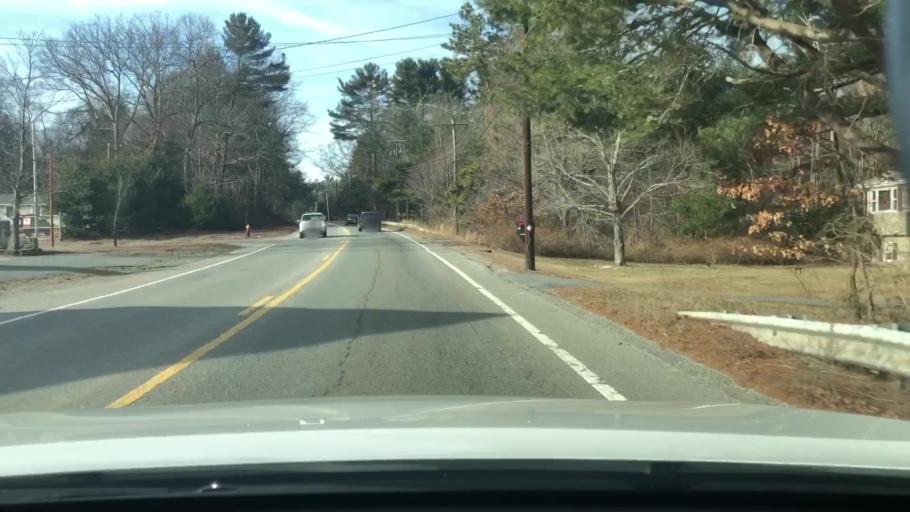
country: US
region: Massachusetts
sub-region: Worcester County
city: Northbridge
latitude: 42.1755
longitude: -71.6336
